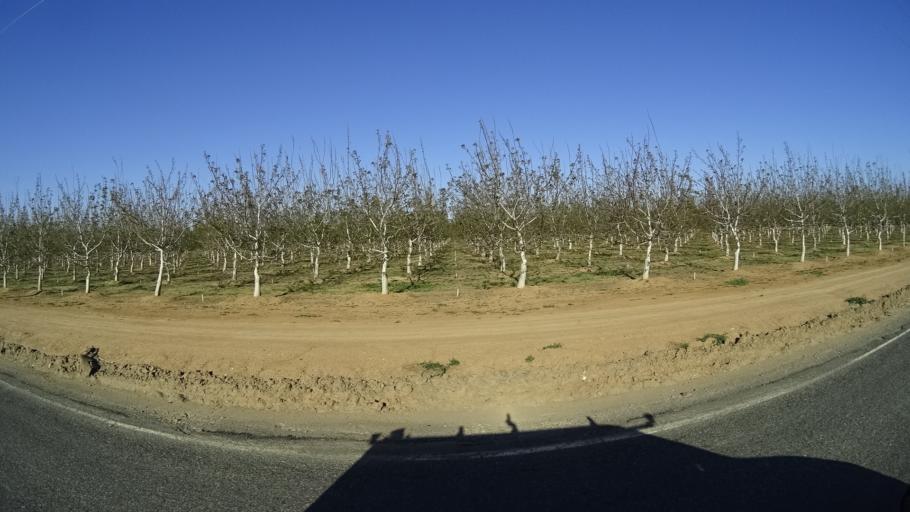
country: US
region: California
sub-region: Glenn County
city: Orland
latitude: 39.7061
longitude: -122.1783
